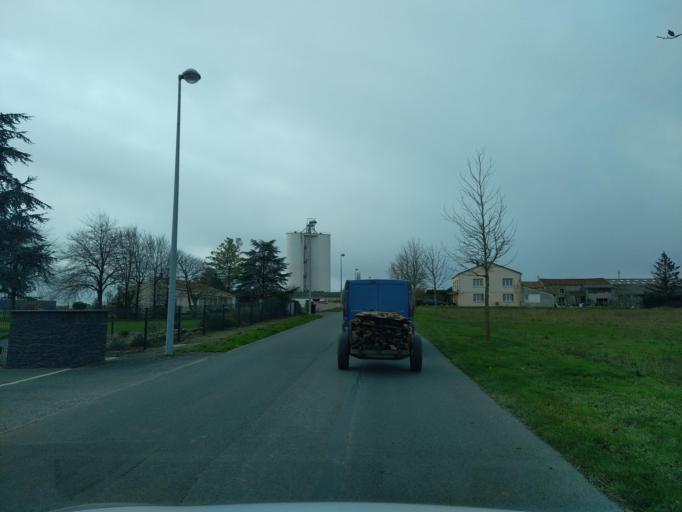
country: FR
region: Pays de la Loire
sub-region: Departement de la Vendee
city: Vix
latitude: 46.3681
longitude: -0.8683
